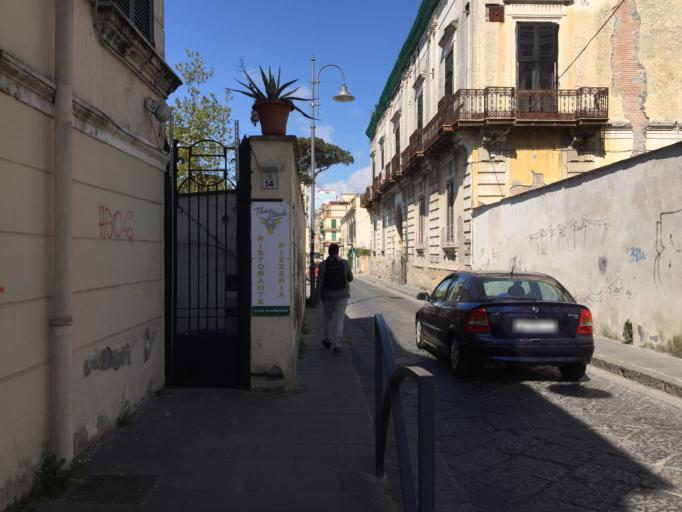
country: IT
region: Campania
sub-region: Provincia di Napoli
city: San Giorgio a Cremano
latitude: 40.8286
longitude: 14.3392
